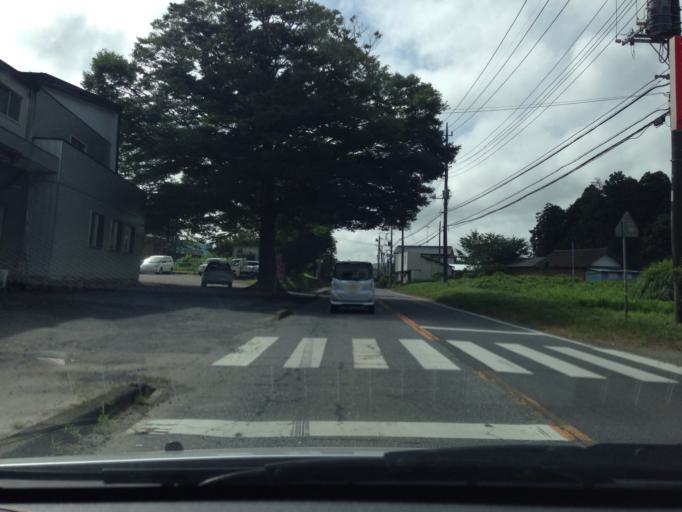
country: JP
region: Ibaraki
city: Inashiki
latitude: 36.0113
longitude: 140.3010
